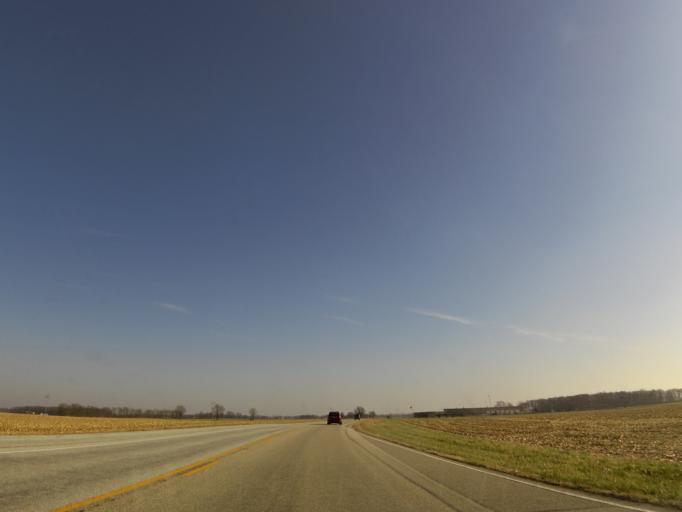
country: US
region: Indiana
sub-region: Shelby County
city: Morristown
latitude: 39.5729
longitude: -85.6099
